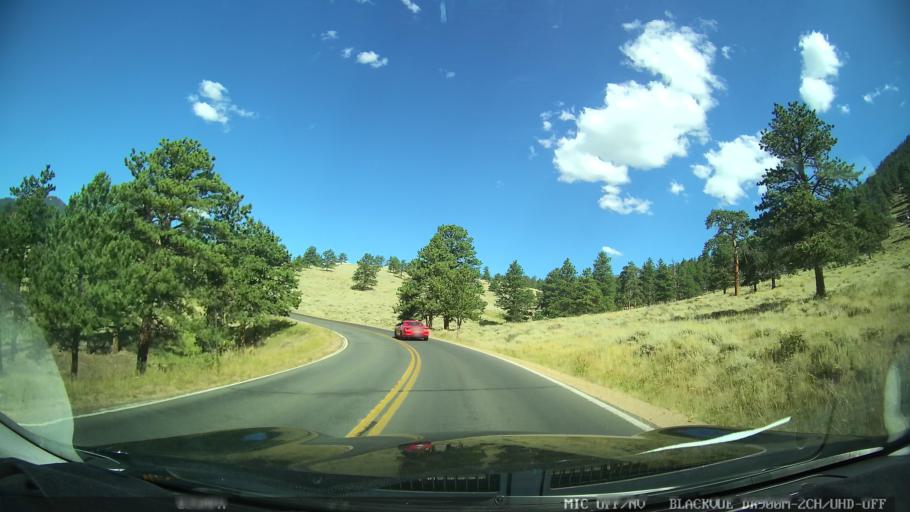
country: US
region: Colorado
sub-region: Larimer County
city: Estes Park
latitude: 40.3813
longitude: -105.6003
